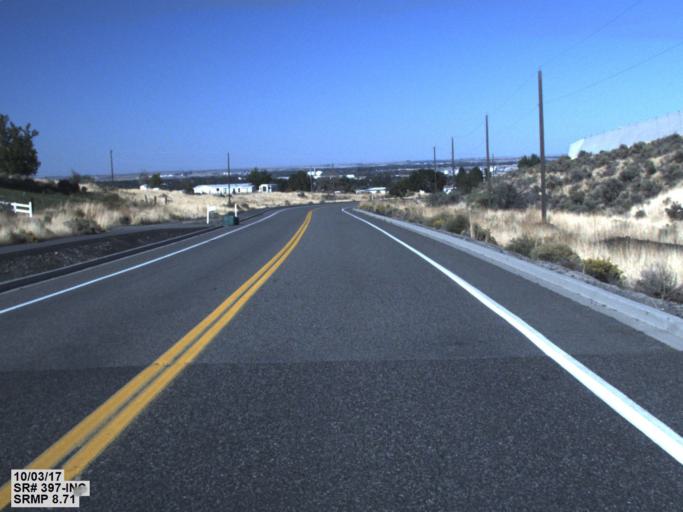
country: US
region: Washington
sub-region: Benton County
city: Finley
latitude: 46.1268
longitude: -119.0407
